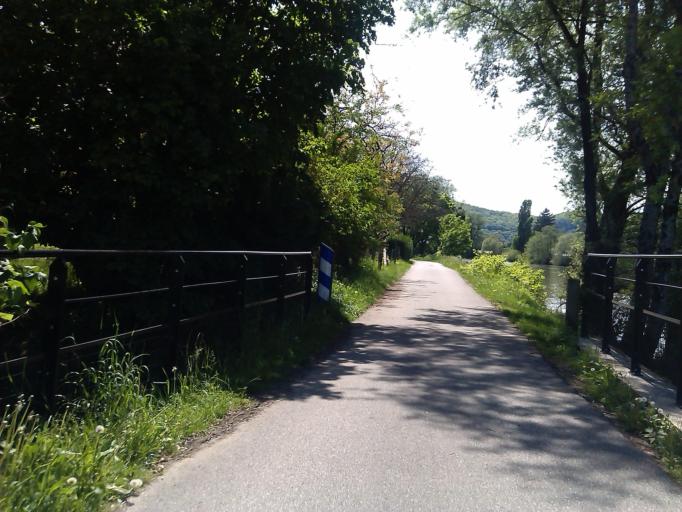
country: FR
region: Franche-Comte
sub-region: Departement du Doubs
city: Beure
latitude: 47.2097
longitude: 5.9969
